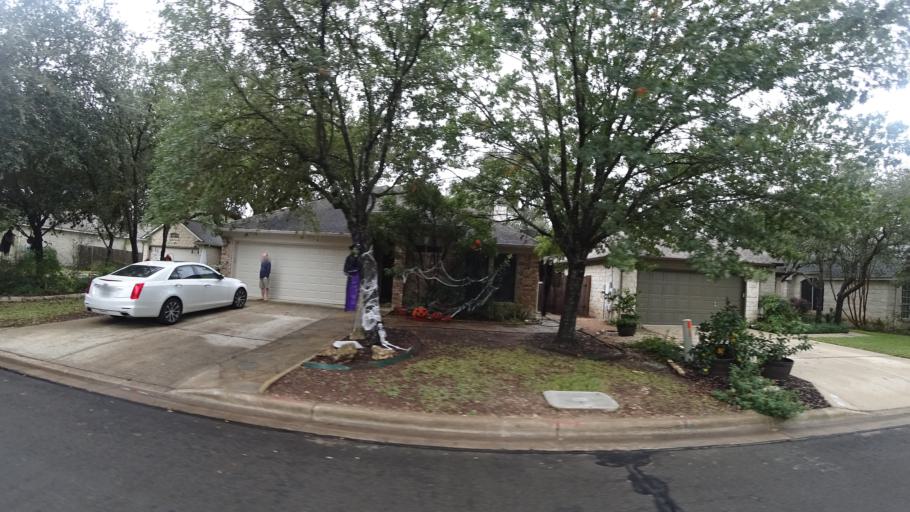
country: US
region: Texas
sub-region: Travis County
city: Shady Hollow
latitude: 30.1883
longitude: -97.8694
